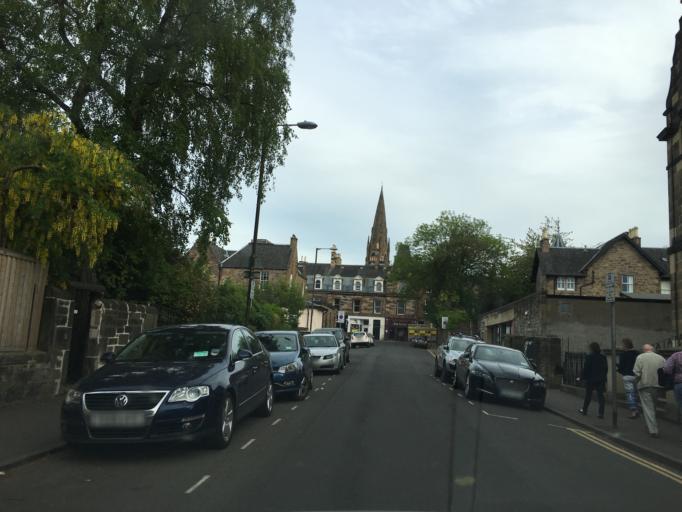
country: GB
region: Scotland
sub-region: Edinburgh
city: Edinburgh
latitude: 55.9346
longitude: -3.2120
